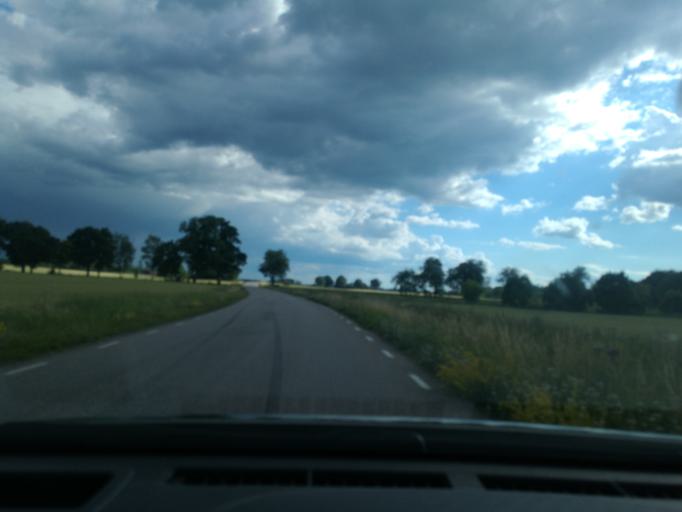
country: SE
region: Soedermanland
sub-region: Eskilstuna Kommun
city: Arla
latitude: 59.4444
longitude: 16.7201
